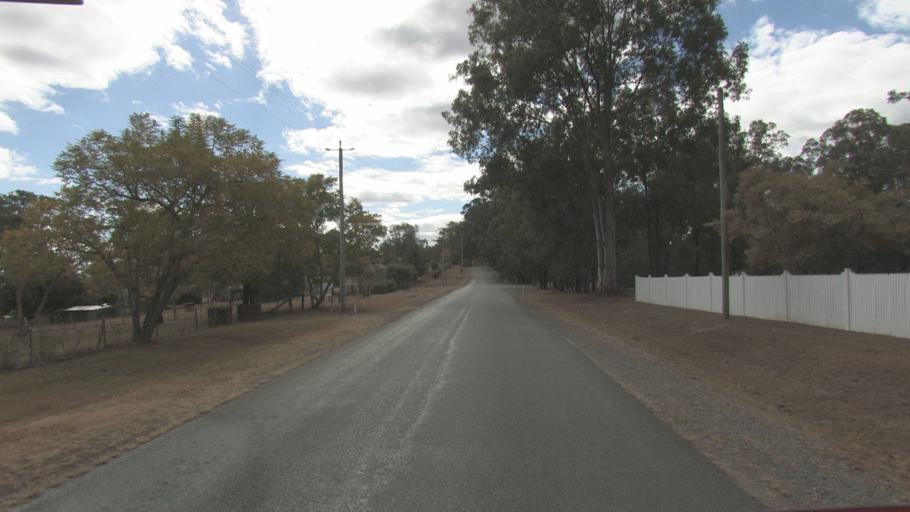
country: AU
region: Queensland
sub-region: Logan
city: Cedar Vale
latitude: -27.8796
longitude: 153.0278
